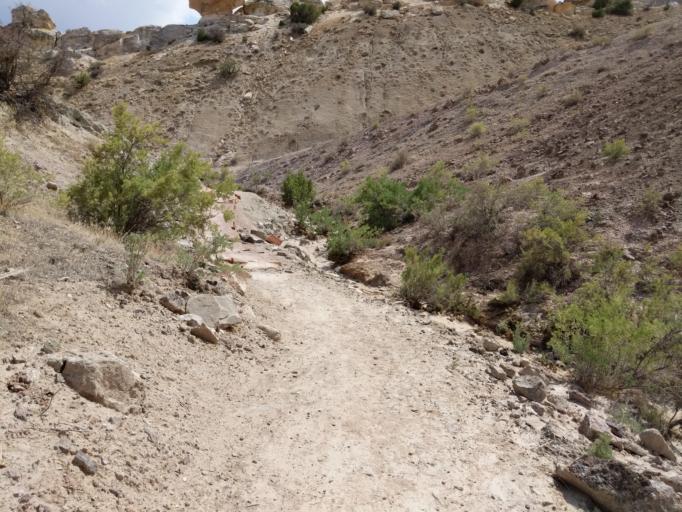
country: US
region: Utah
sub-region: Uintah County
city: Naples
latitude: 40.4398
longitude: -109.2993
